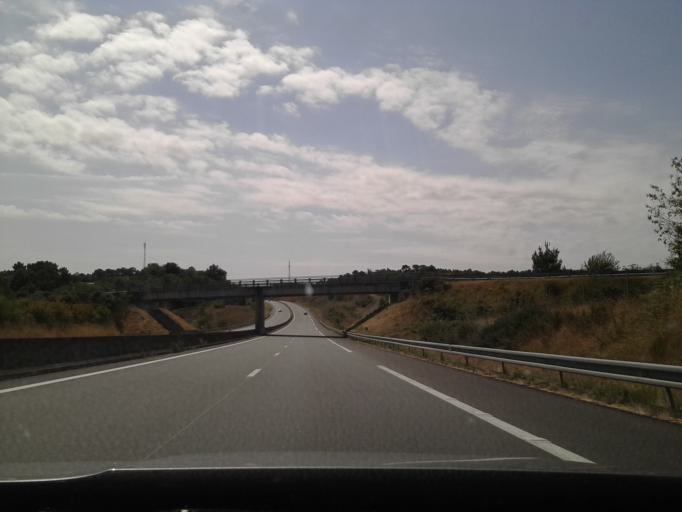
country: FR
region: Pays de la Loire
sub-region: Departement de la Sarthe
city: Luceau
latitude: 47.7142
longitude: 0.3461
